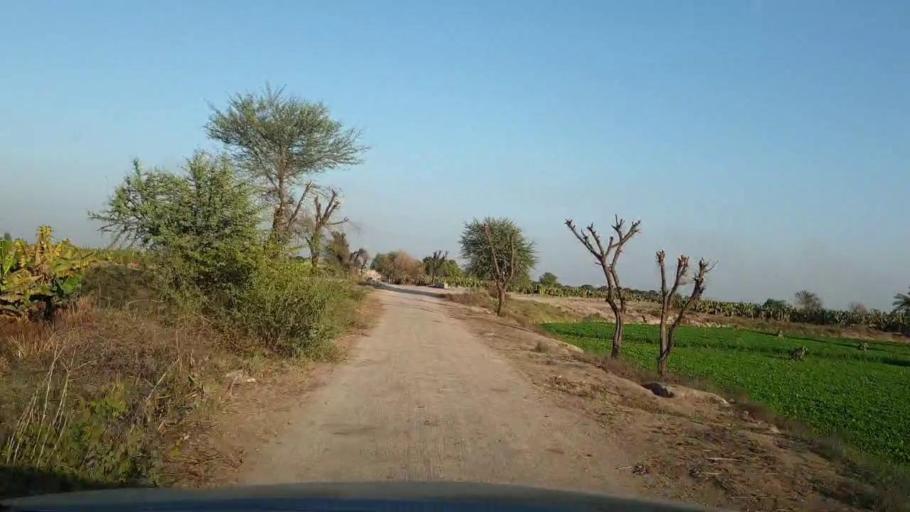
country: PK
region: Sindh
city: Matiari
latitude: 25.6168
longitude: 68.5977
